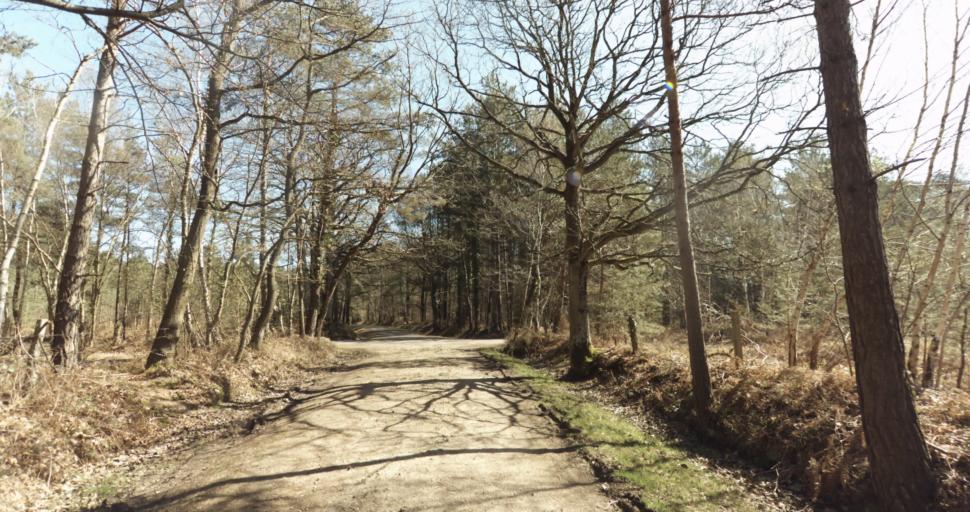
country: FR
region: Lower Normandy
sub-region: Departement du Calvados
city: Saint-Pierre-sur-Dives
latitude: 49.0040
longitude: 0.0575
